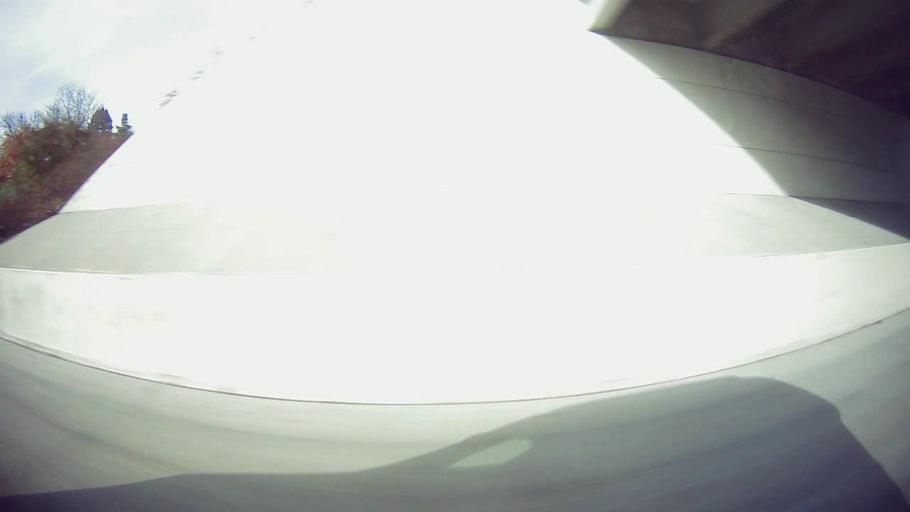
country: US
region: Michigan
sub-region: Wayne County
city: Redford
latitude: 42.3855
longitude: -83.2809
